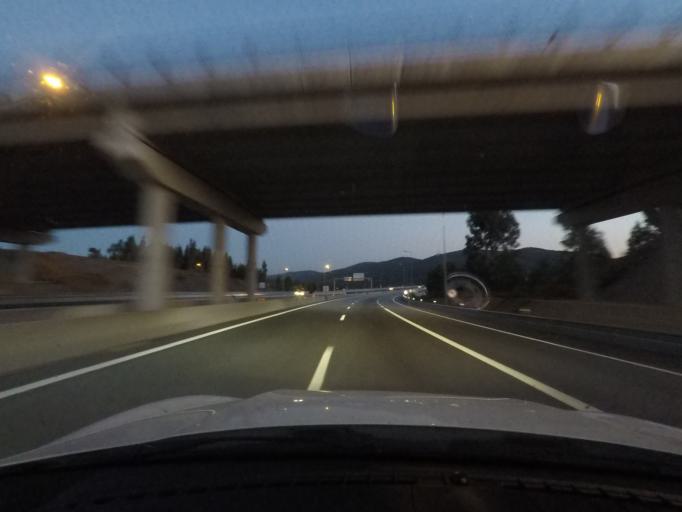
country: PT
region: Porto
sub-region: Paredes
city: Recarei
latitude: 41.1387
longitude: -8.4263
